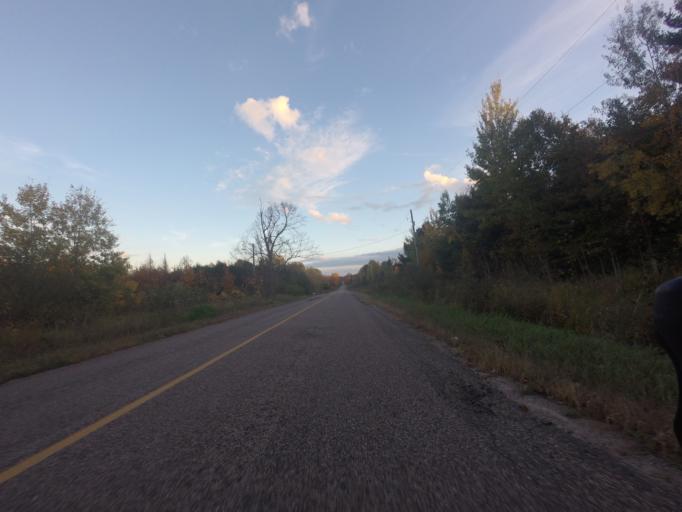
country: CA
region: Ontario
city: Renfrew
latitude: 45.4351
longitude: -76.9617
